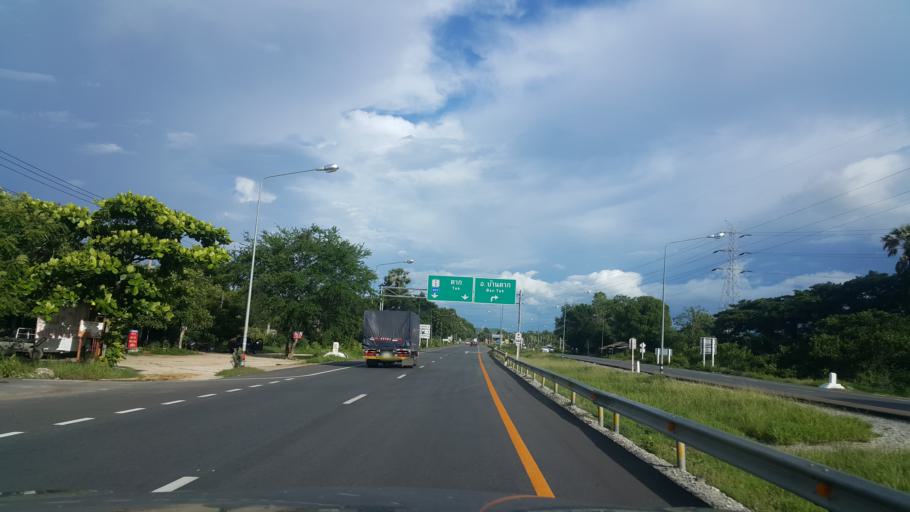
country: TH
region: Tak
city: Ban Tak
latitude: 17.0374
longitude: 99.0864
